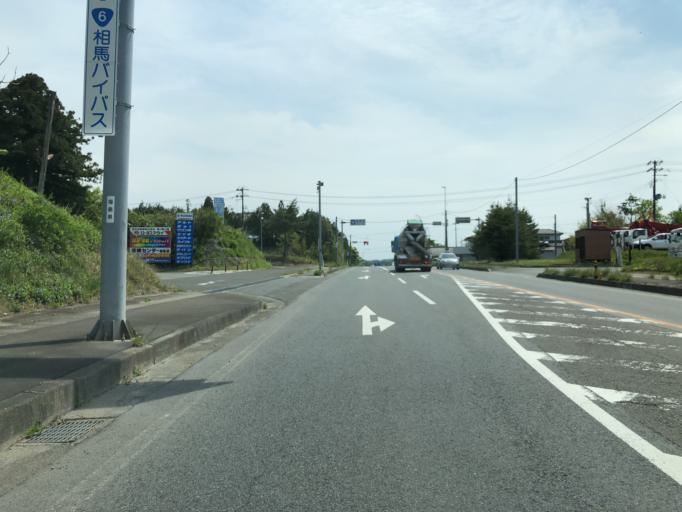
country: JP
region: Miyagi
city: Marumori
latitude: 37.8380
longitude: 140.9182
